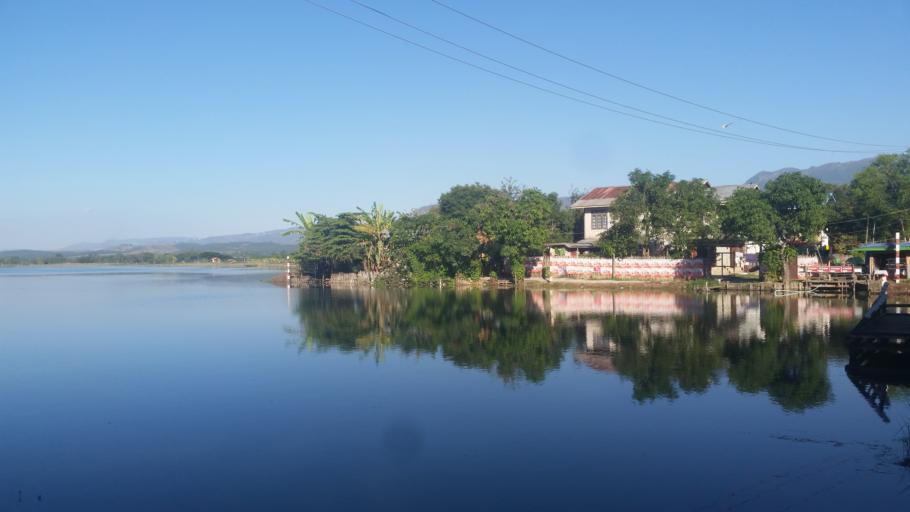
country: MM
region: Shan
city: Taunggyi
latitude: 20.6643
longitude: 96.9312
